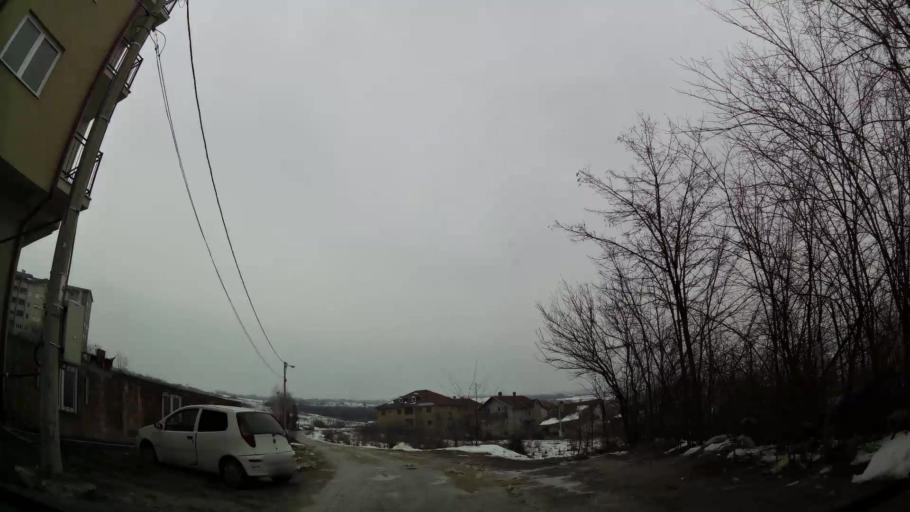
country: RS
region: Central Serbia
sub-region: Belgrade
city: Zvezdara
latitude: 44.7593
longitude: 20.5051
